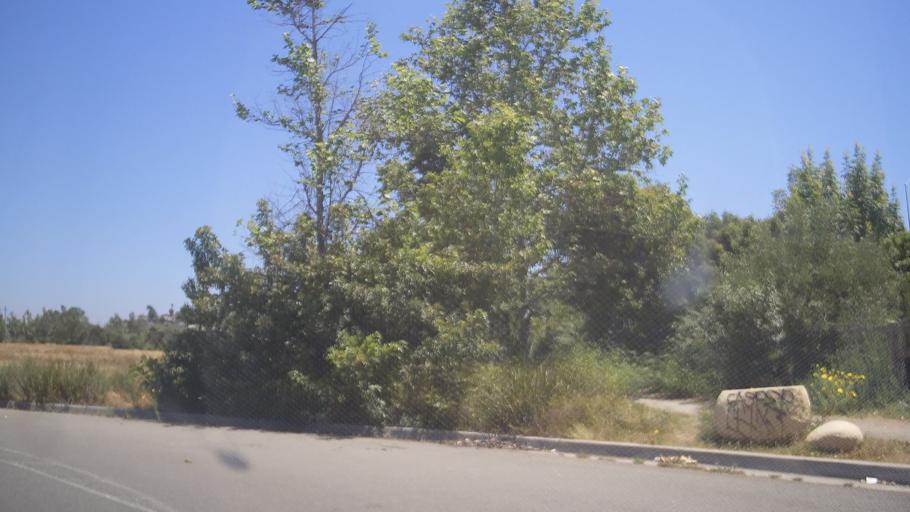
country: US
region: California
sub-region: San Diego County
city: National City
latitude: 32.7086
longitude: -117.0765
